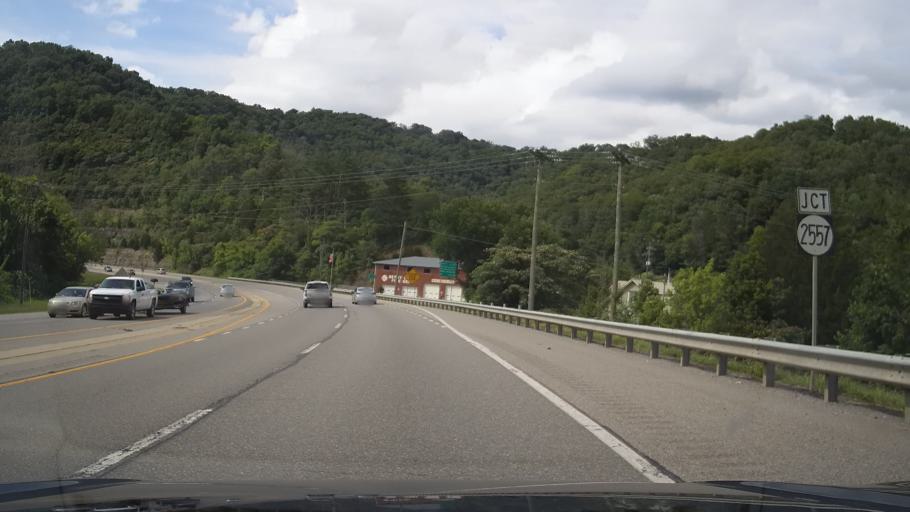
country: US
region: Kentucky
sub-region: Pike County
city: Coal Run Village
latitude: 37.5551
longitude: -82.6304
